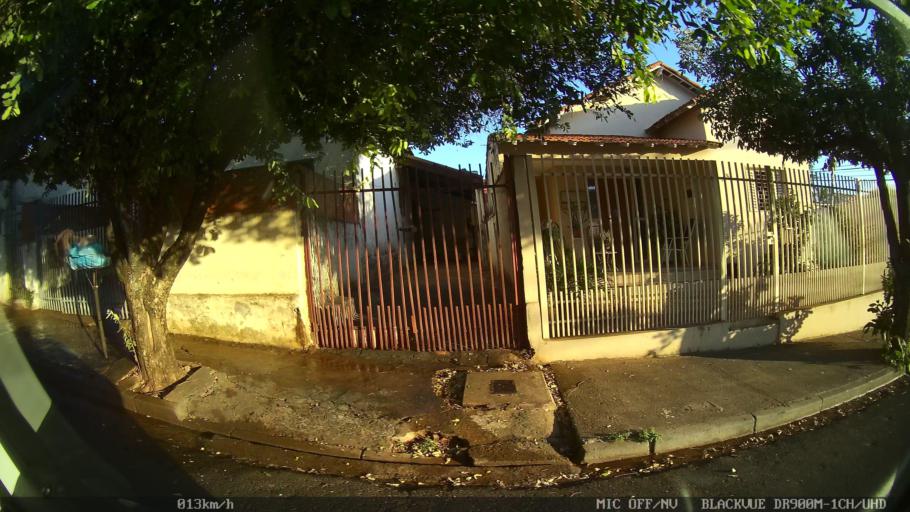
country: BR
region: Sao Paulo
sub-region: Sao Jose Do Rio Preto
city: Sao Jose do Rio Preto
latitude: -20.7966
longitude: -49.3747
